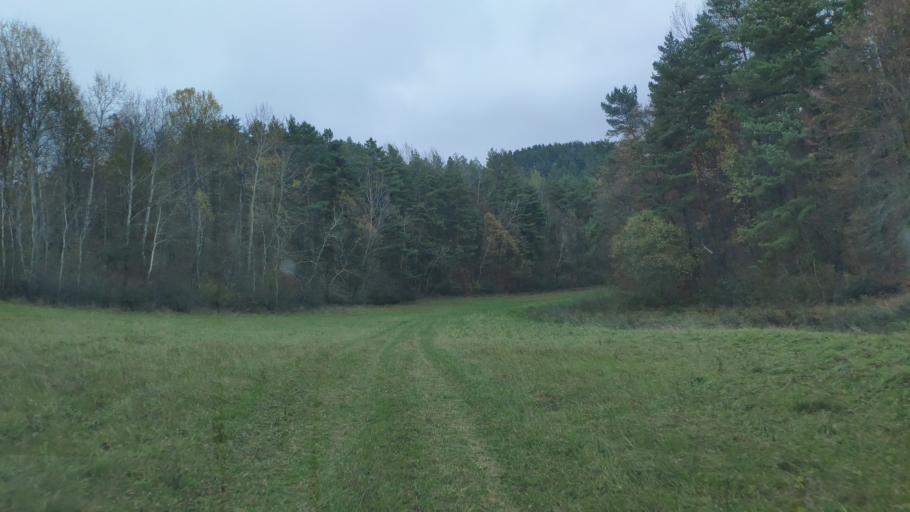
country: SK
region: Presovsky
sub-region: Okres Presov
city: Presov
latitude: 48.9301
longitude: 21.1013
